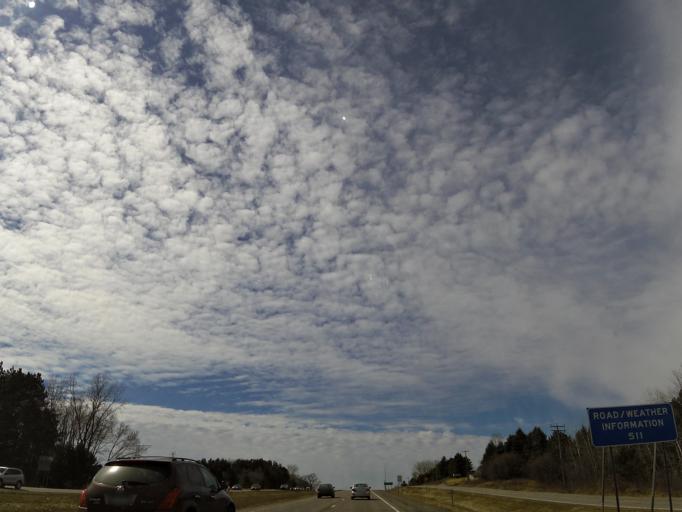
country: US
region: Minnesota
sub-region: Washington County
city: Lake Elmo
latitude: 45.0360
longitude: -92.8668
